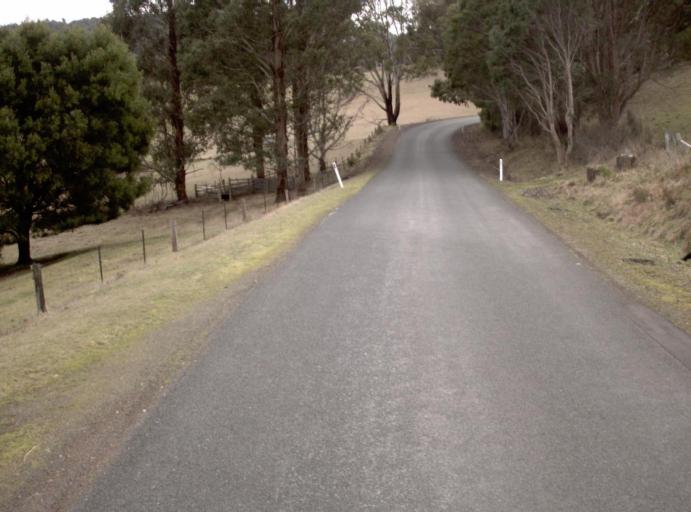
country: AU
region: Tasmania
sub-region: Dorset
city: Scottsdale
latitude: -41.4585
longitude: 147.5959
